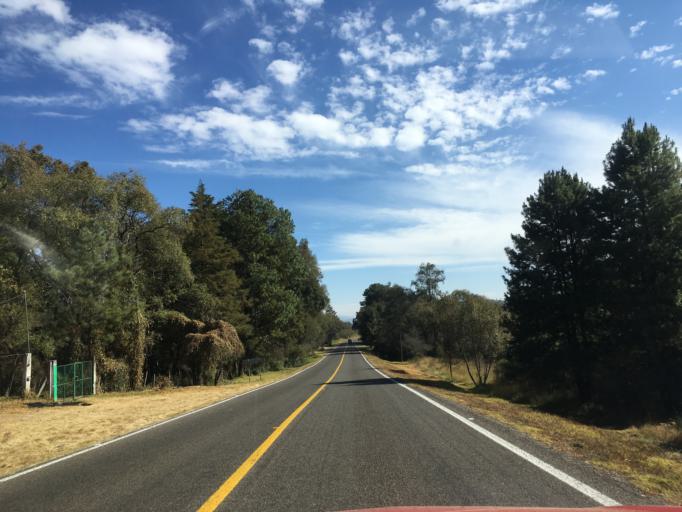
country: MX
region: Michoacan
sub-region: Hidalgo
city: Tierras Coloradas (San Pedro)
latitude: 19.6671
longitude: -100.7126
